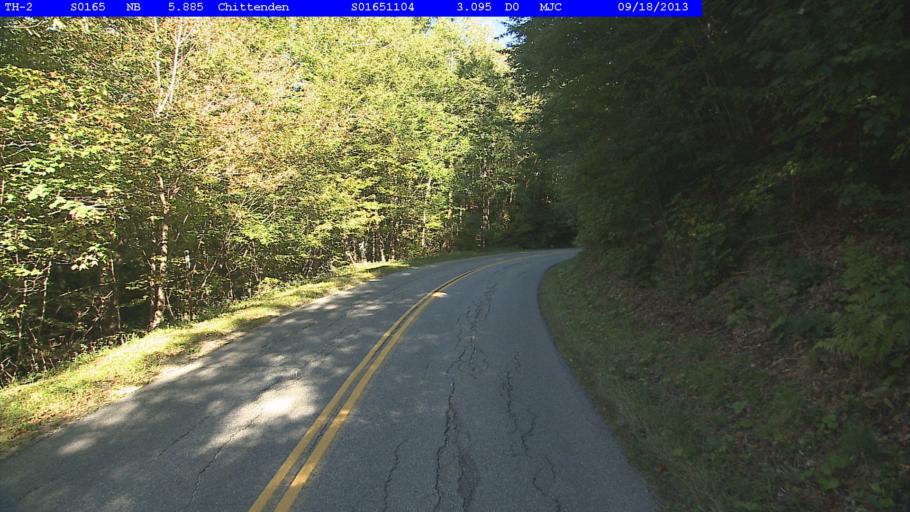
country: US
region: Vermont
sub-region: Rutland County
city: Rutland
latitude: 43.7195
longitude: -72.9649
